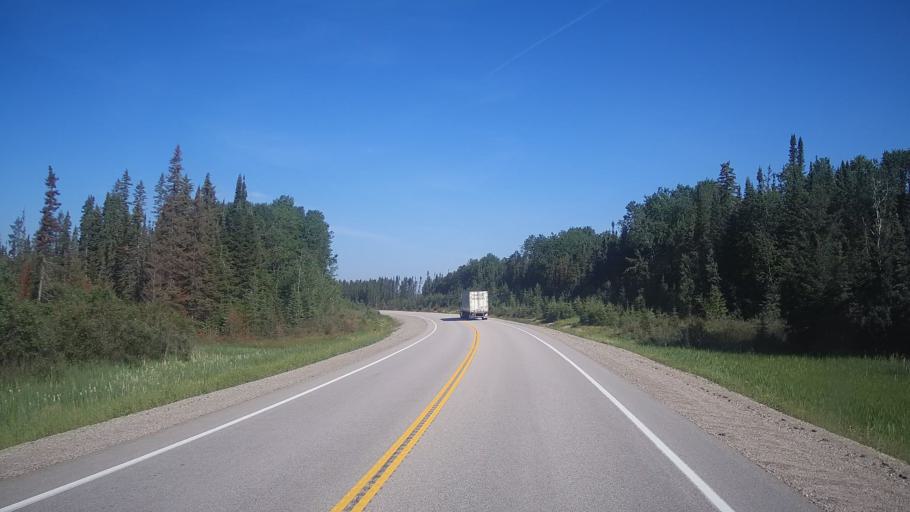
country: CA
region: Ontario
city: Dryden
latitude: 49.5863
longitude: -92.2664
